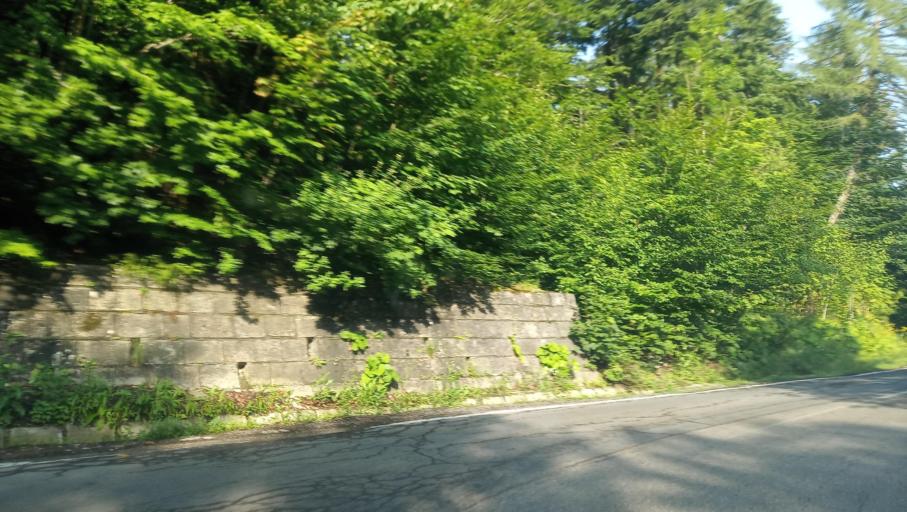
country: RO
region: Prahova
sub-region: Oras Sinaia
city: Sinaia
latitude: 45.3273
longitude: 25.5210
